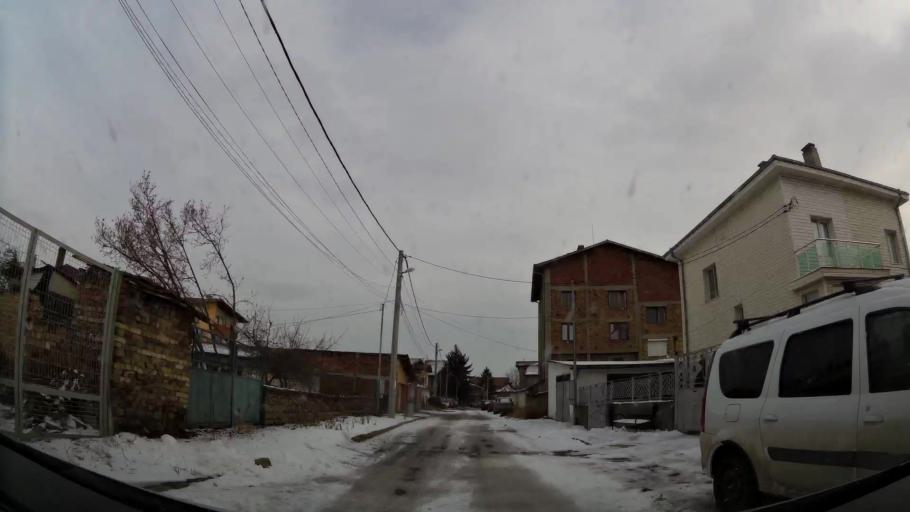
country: BG
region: Sofia-Capital
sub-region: Stolichna Obshtina
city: Sofia
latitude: 42.7154
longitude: 23.4081
